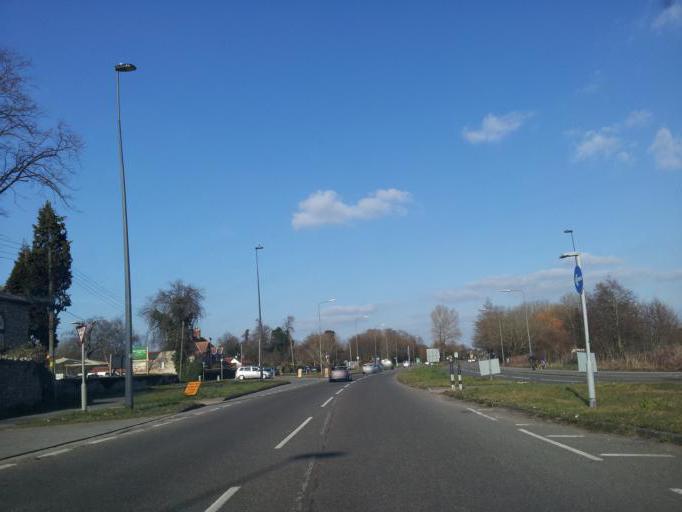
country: GB
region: England
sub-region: South Gloucestershire
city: Almondsbury
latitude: 51.5253
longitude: -2.6151
